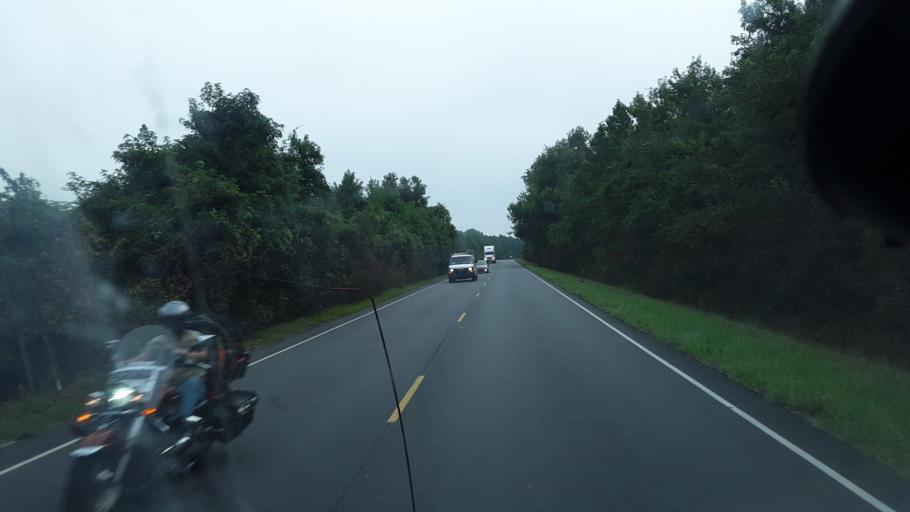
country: US
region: South Carolina
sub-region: Florence County
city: Johnsonville
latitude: 33.8979
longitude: -79.4431
